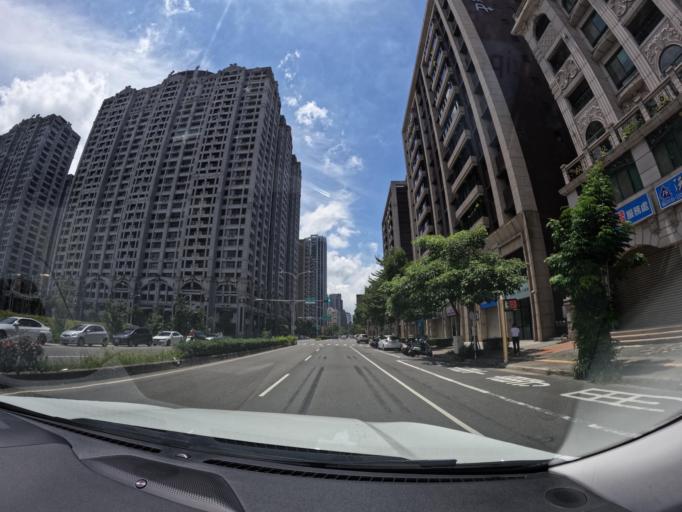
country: TW
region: Taipei
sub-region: Taipei
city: Banqiao
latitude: 25.0865
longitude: 121.3789
